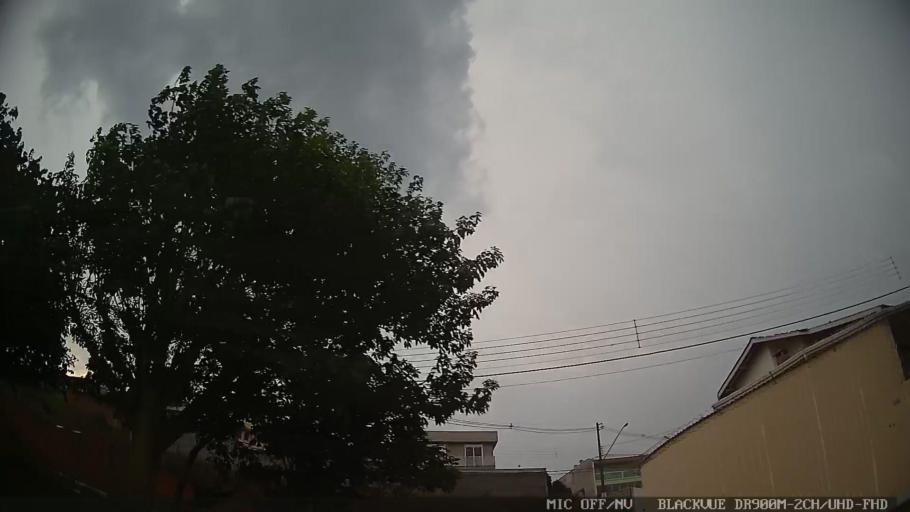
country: BR
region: Sao Paulo
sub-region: Braganca Paulista
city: Braganca Paulista
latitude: -22.9631
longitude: -46.5446
